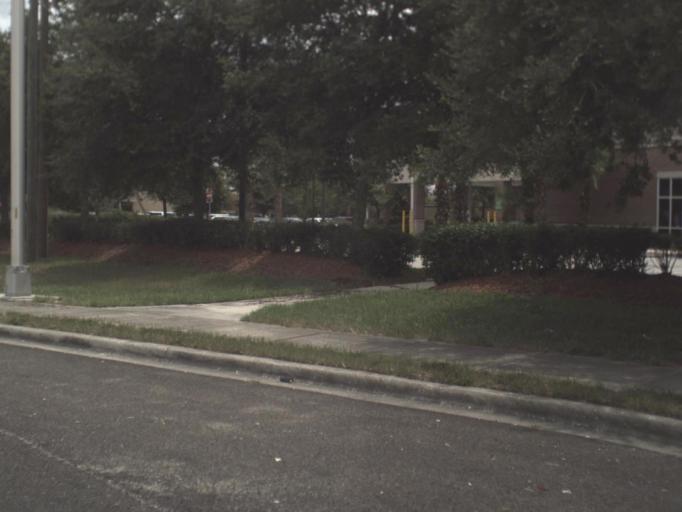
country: US
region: Florida
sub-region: Pasco County
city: Trinity
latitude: 28.2059
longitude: -82.6653
